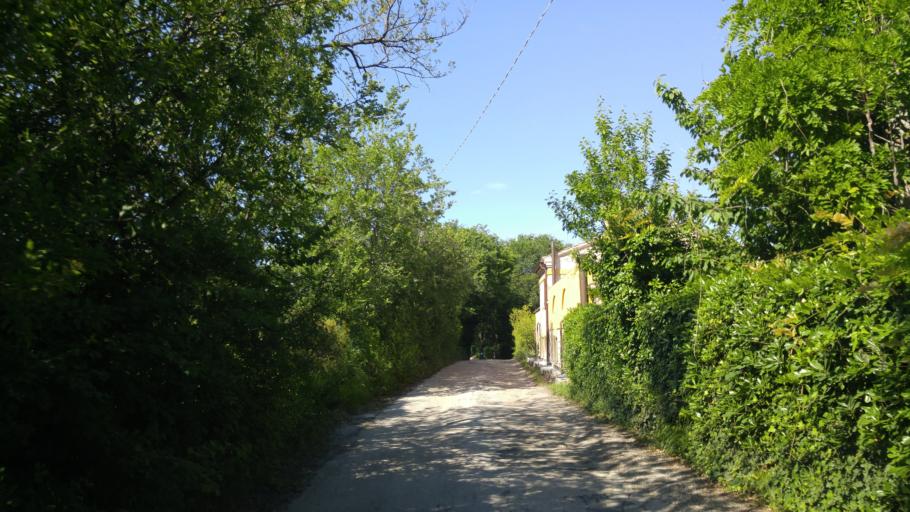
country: IT
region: The Marches
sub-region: Provincia di Pesaro e Urbino
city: Centinarola
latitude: 43.8452
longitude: 12.9901
